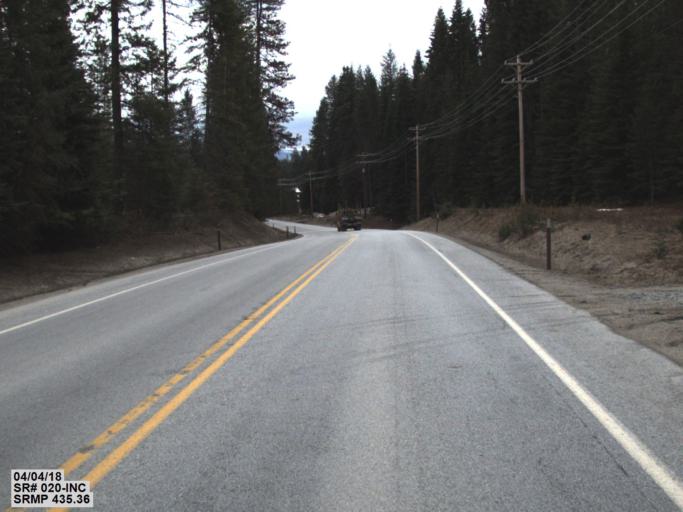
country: US
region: Washington
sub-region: Pend Oreille County
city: Newport
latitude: 48.2015
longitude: -117.0627
